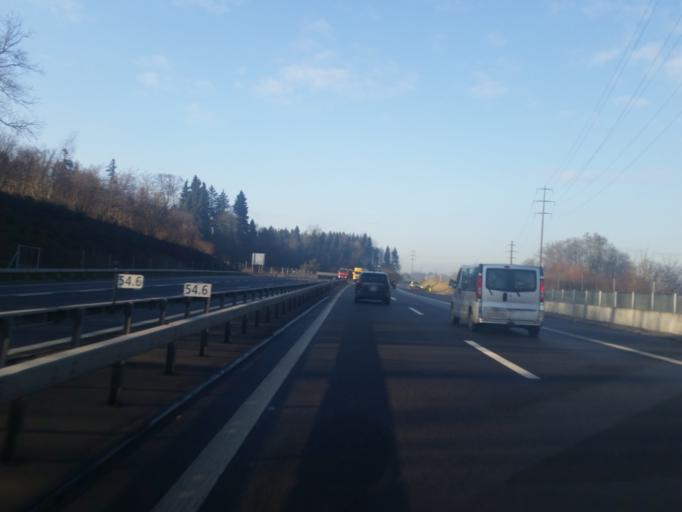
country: CH
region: Zurich
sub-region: Bezirk Affoltern
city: Knonau
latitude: 47.2285
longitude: 8.4618
